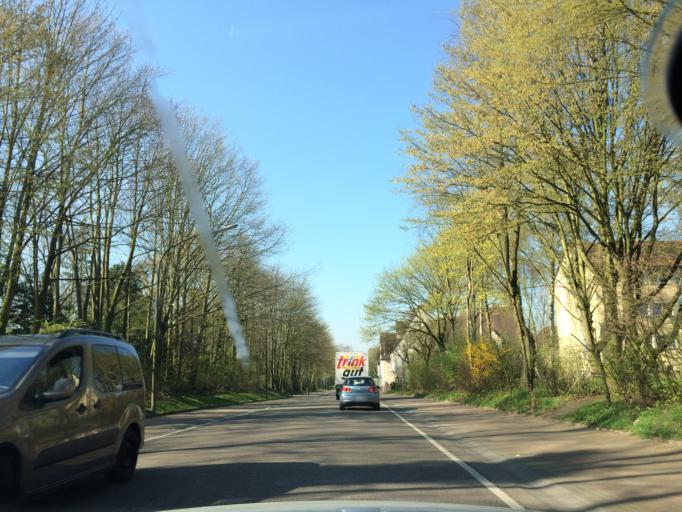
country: DE
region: North Rhine-Westphalia
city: Herten
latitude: 51.5722
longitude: 7.0905
